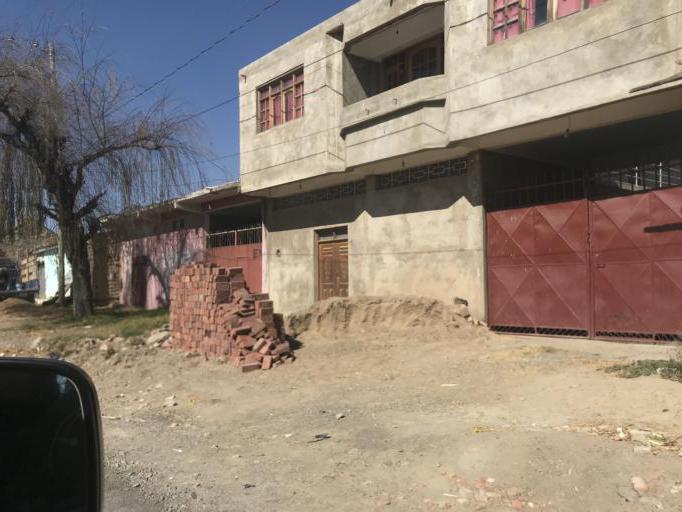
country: BO
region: Cochabamba
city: Punata
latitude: -17.5535
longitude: -65.8542
